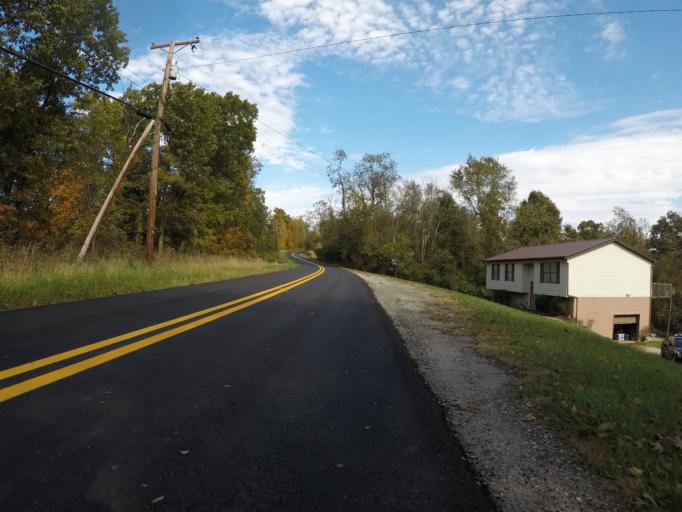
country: US
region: West Virginia
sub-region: Cabell County
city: Huntington
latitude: 38.3734
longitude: -82.4292
